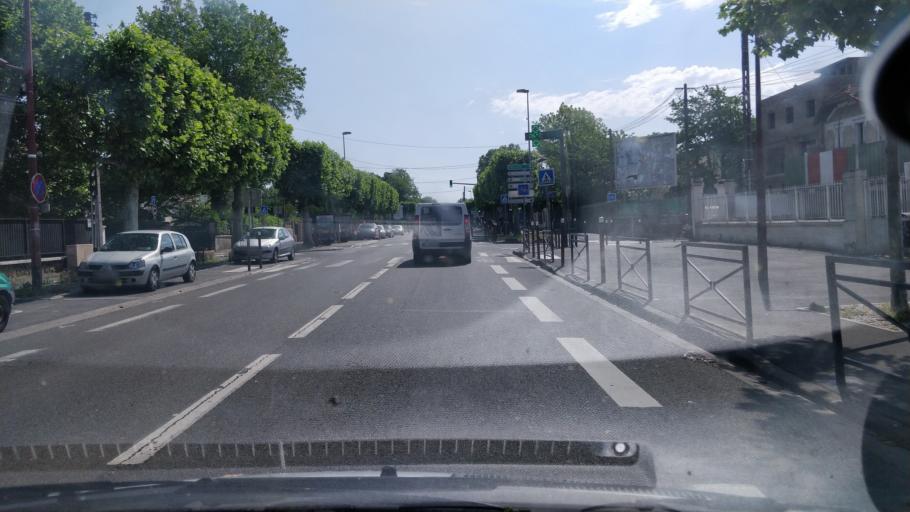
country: FR
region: Ile-de-France
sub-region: Departement de Seine-Saint-Denis
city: Clichy-sous-Bois
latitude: 48.8985
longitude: 2.5513
